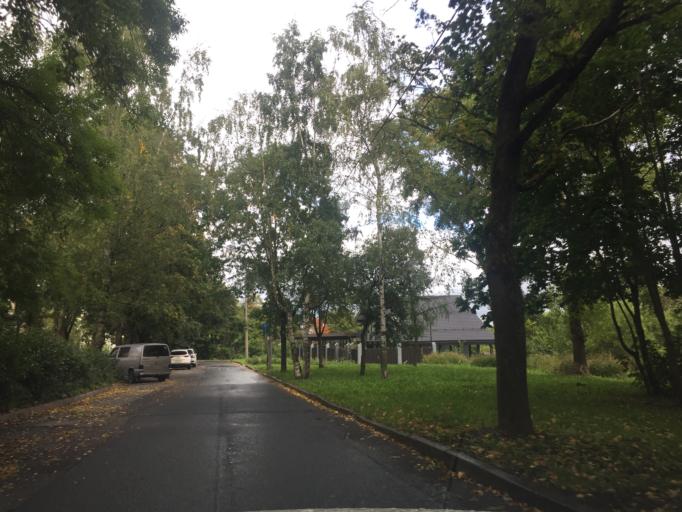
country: RU
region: St.-Petersburg
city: Krasnoye Selo
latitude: 59.7360
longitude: 30.0922
